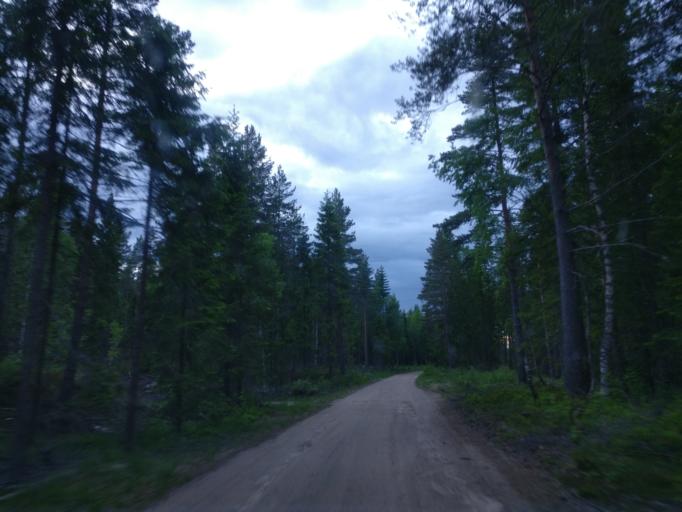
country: SE
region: Vaesternorrland
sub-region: Sundsvalls Kommun
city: Njurundabommen
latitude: 62.2052
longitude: 17.3499
